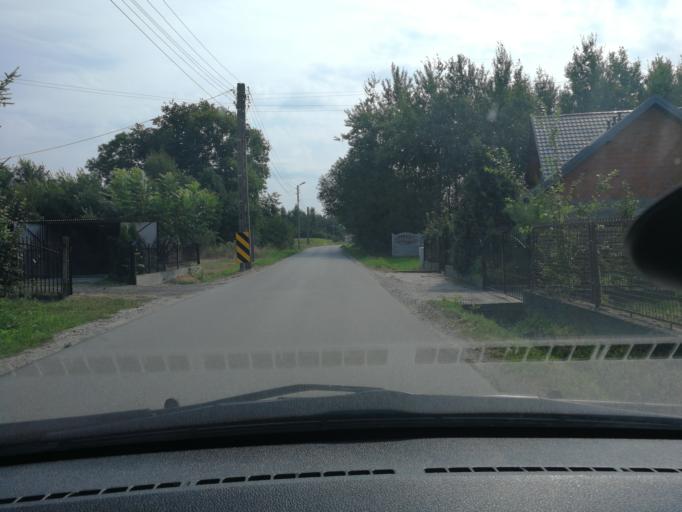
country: PL
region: Lodz Voivodeship
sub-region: Skierniewice
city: Skierniewice
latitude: 51.9743
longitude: 20.1093
